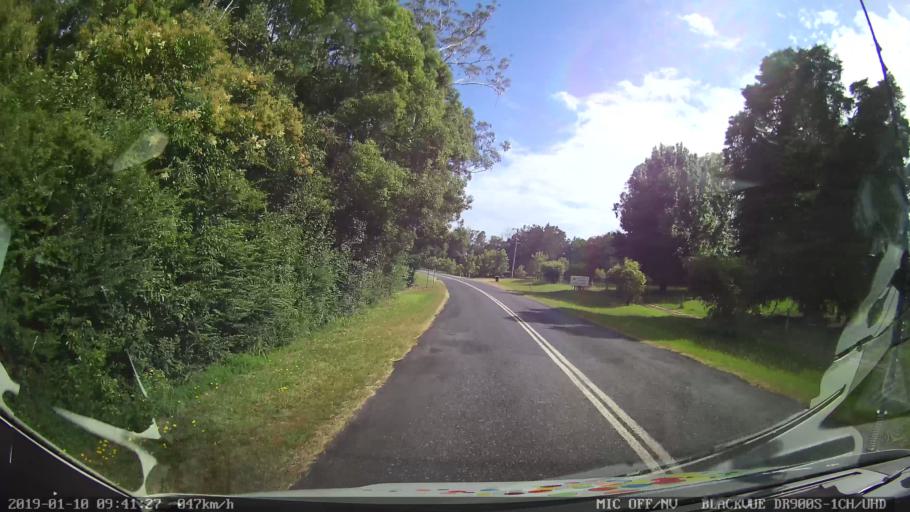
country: AU
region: New South Wales
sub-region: Coffs Harbour
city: Nana Glen
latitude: -30.1422
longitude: 153.0080
